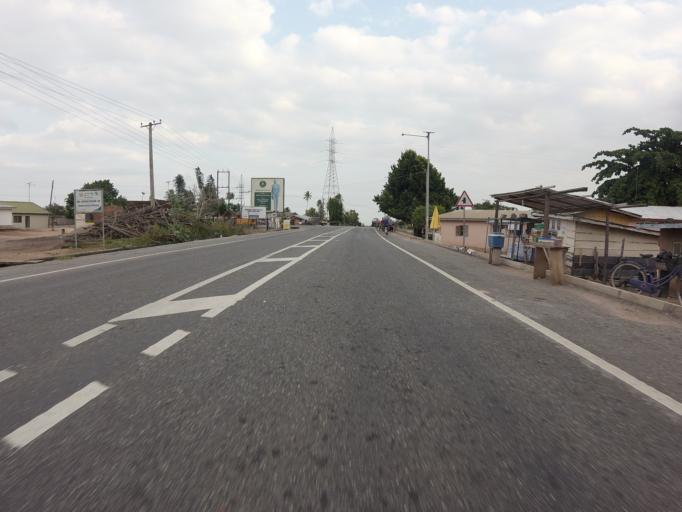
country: GH
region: Volta
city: Ho
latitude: 6.2610
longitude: 0.5487
